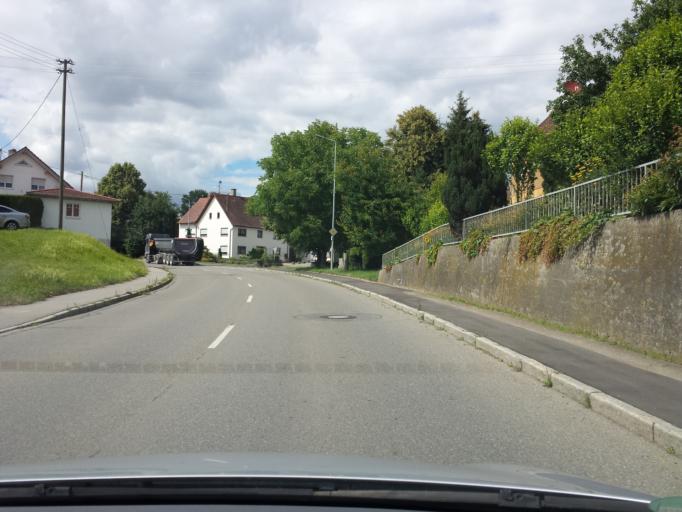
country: DE
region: Baden-Wuerttemberg
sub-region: Tuebingen Region
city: Burgrieden
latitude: 48.2273
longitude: 9.9514
